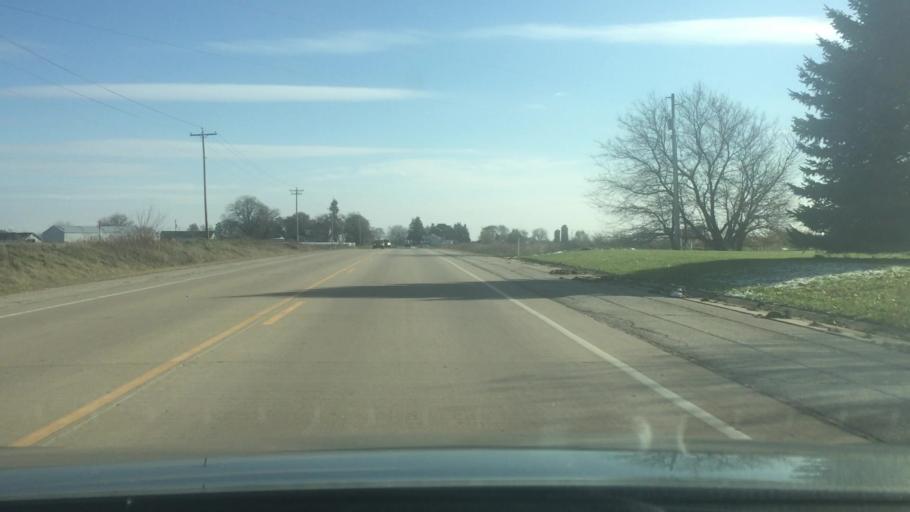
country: US
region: Wisconsin
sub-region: Jefferson County
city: Fort Atkinson
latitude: 42.9537
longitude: -88.8825
